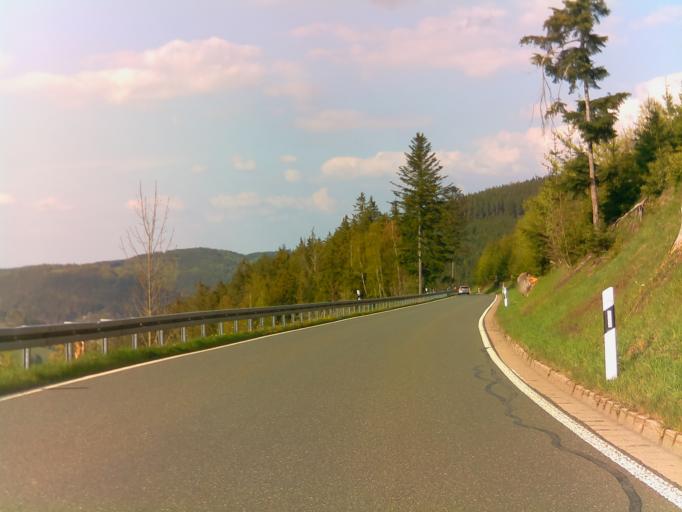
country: DE
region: Thuringia
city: Grafenthal
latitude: 50.5036
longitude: 11.2906
